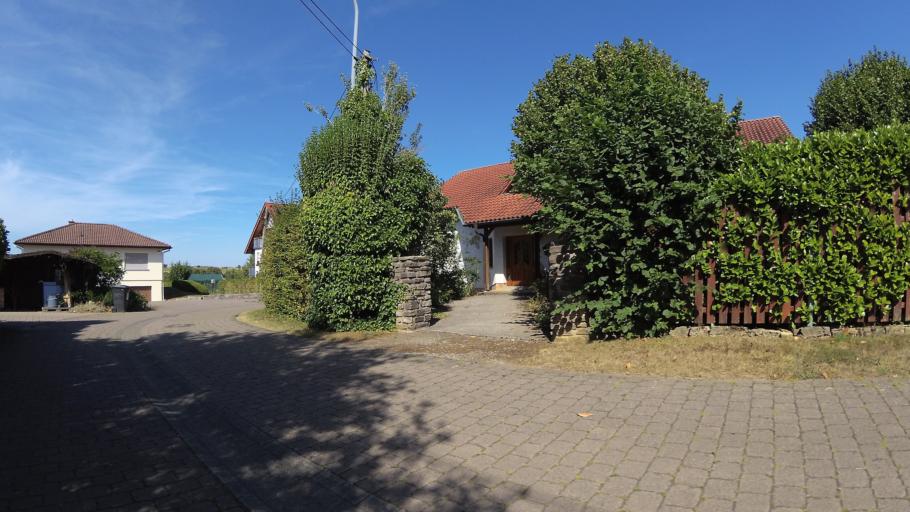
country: DE
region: Saarland
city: Gersheim
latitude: 49.1443
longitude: 7.2818
